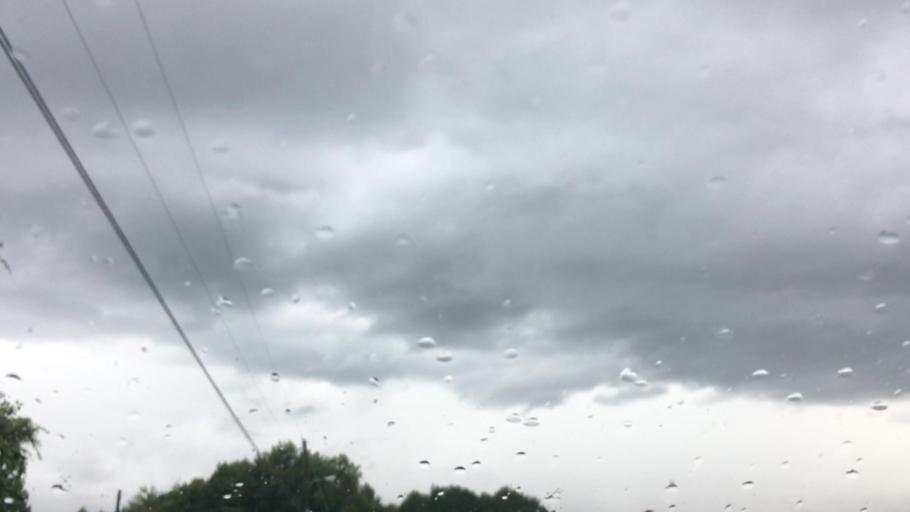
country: US
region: Alabama
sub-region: Tuscaloosa County
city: Northport
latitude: 33.2422
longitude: -87.5839
